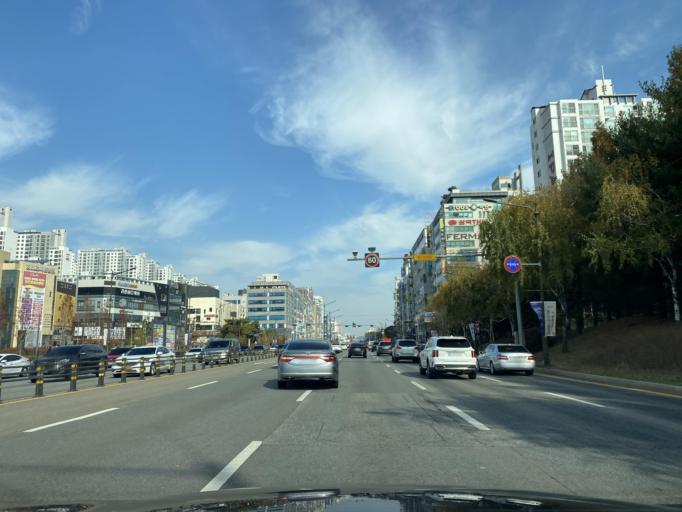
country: KR
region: Chungcheongnam-do
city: Cheonan
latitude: 36.8090
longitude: 127.1077
